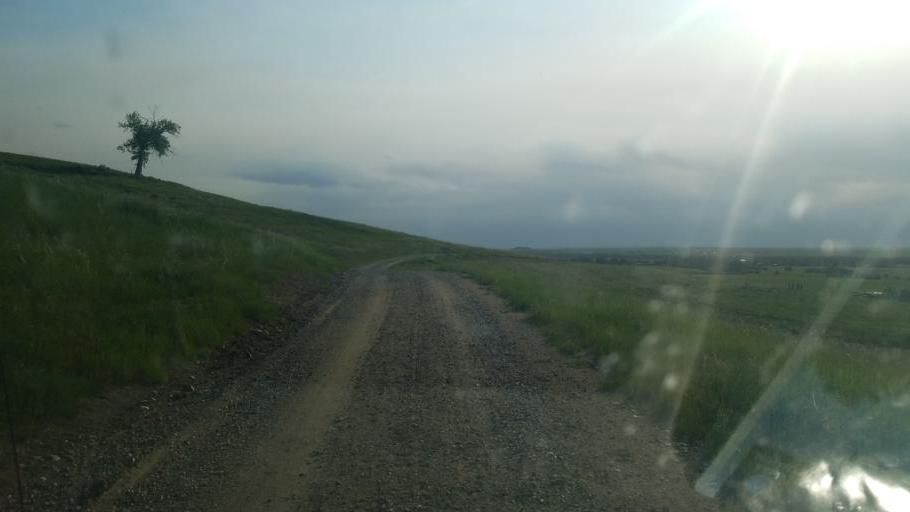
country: US
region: Montana
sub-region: Carbon County
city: Red Lodge
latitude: 45.3705
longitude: -109.1896
